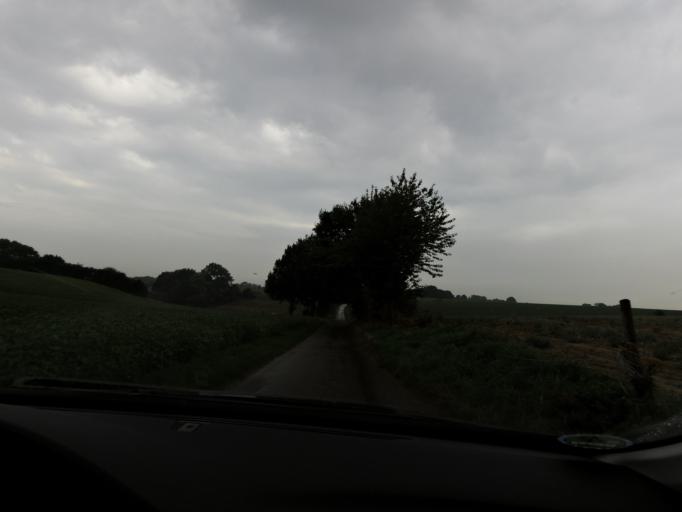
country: NL
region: Limburg
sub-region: Gemeente Voerendaal
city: Ubachsberg
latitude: 50.8356
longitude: 5.9233
